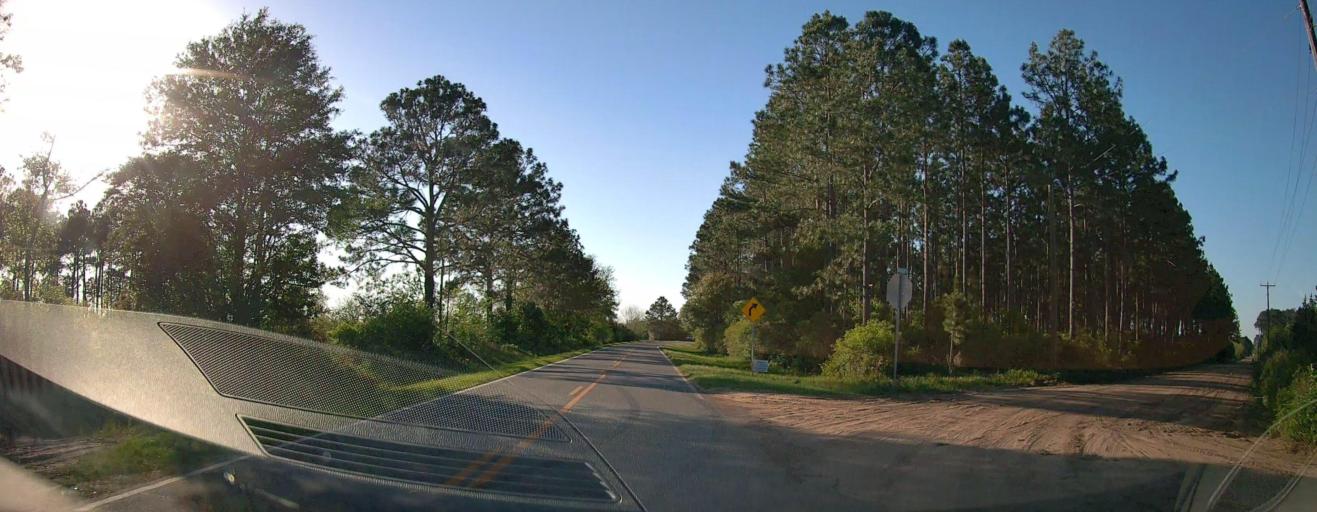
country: US
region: Georgia
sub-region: Ben Hill County
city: Fitzgerald
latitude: 31.6701
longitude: -83.1893
